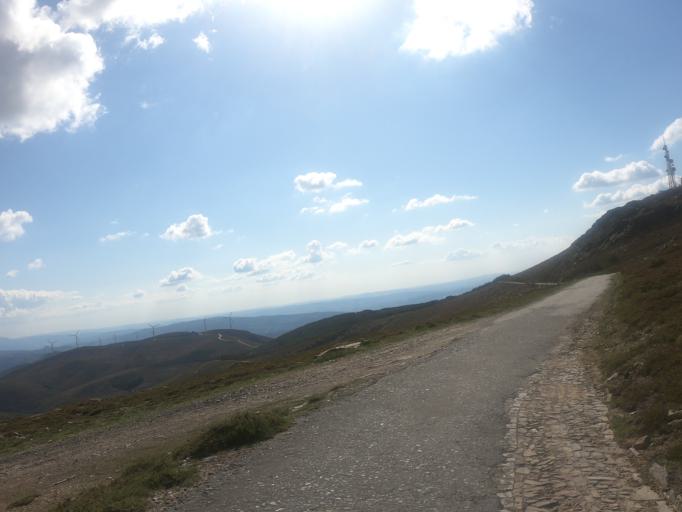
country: PT
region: Vila Real
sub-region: Mesao Frio
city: Mesao Frio
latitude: 41.2459
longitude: -7.8808
